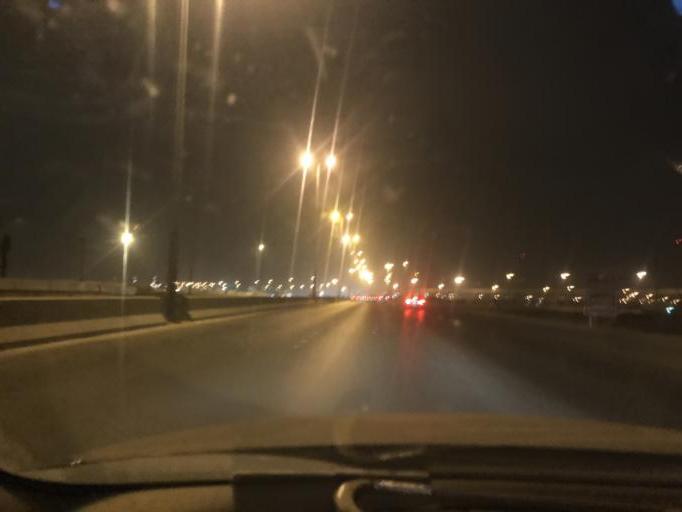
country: SA
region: Ar Riyad
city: Riyadh
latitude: 24.8298
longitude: 46.7267
